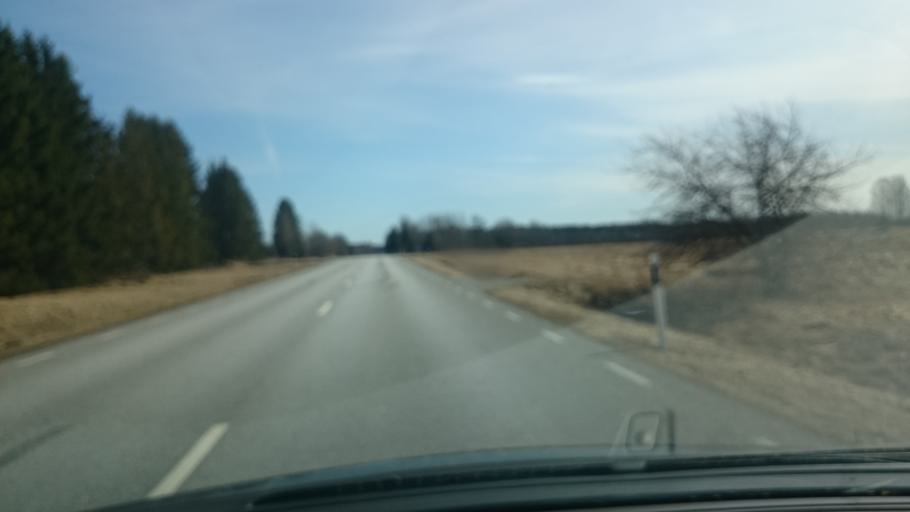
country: EE
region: Paernumaa
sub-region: Tootsi vald
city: Tootsi
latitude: 58.6541
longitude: 24.8437
